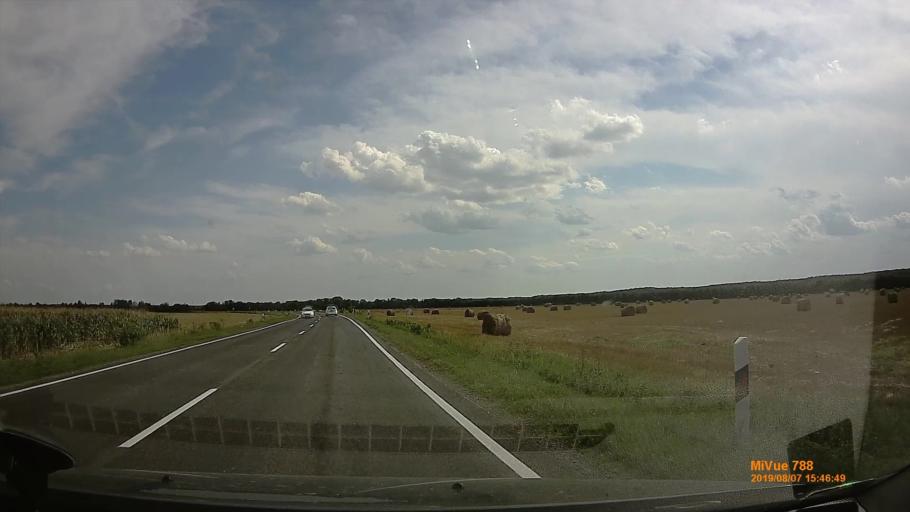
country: HU
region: Vas
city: Szombathely
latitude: 47.1802
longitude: 16.6224
